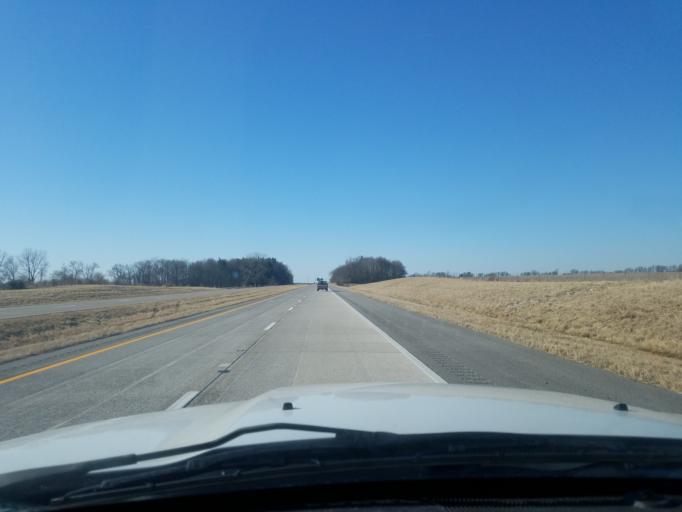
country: US
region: Kentucky
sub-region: Henderson County
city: Henderson
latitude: 37.8064
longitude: -87.5321
